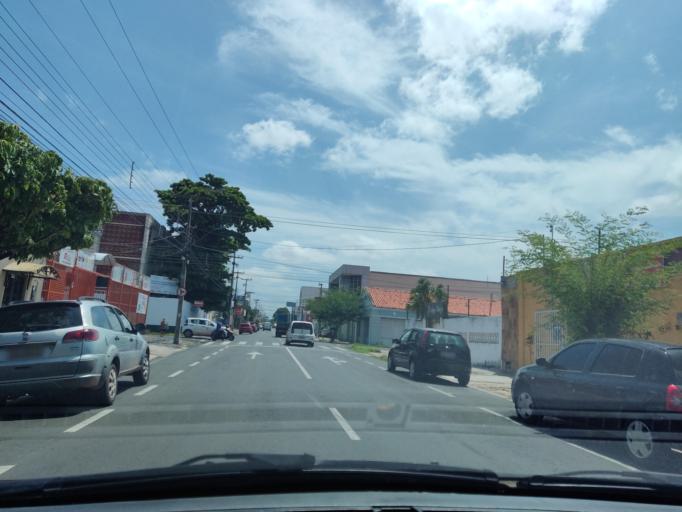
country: BR
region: Piaui
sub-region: Teresina
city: Teresina
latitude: -5.0850
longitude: -42.8171
